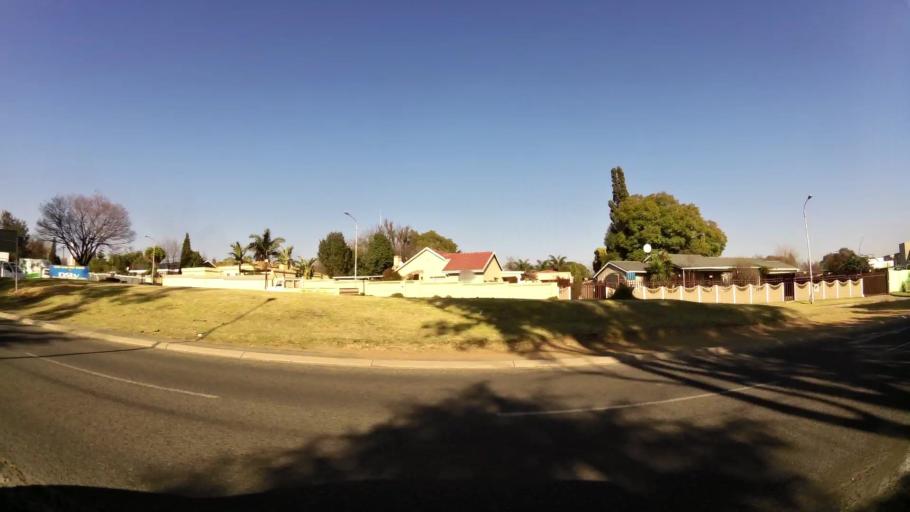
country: ZA
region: Gauteng
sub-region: City of Johannesburg Metropolitan Municipality
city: Modderfontein
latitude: -26.1356
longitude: 28.1564
